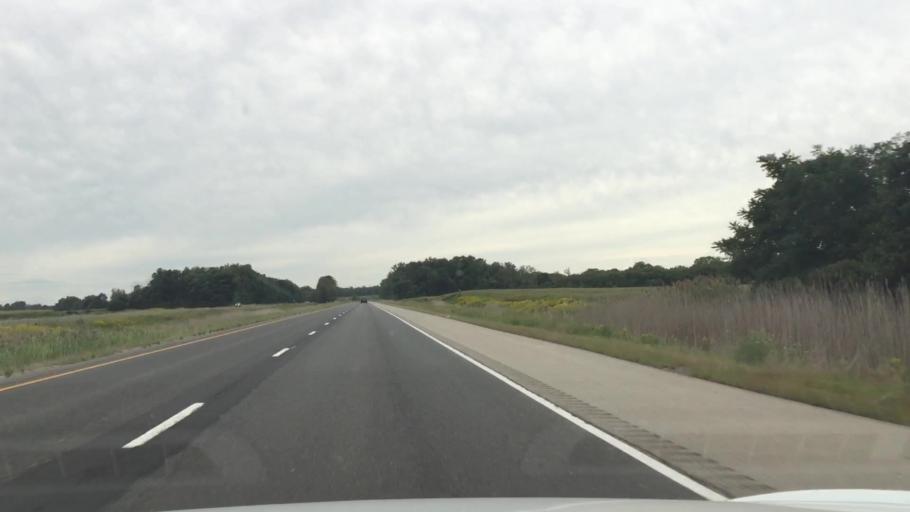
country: CA
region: Ontario
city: Lambton Shores
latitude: 42.9914
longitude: -81.9411
